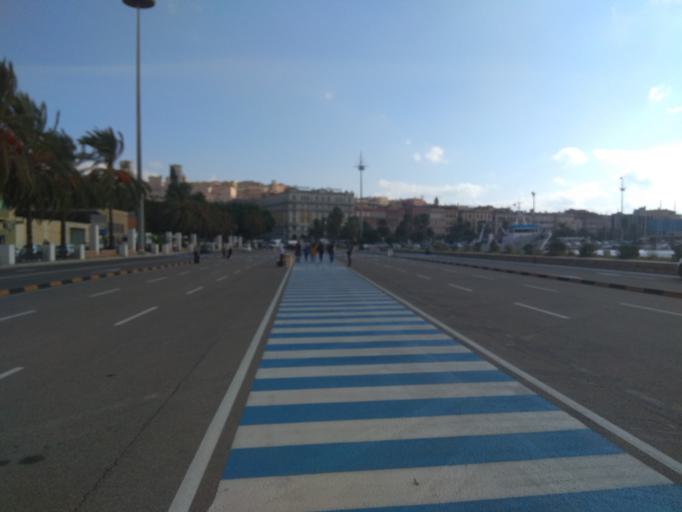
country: IT
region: Sardinia
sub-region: Provincia di Cagliari
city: Cagliari
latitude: 39.2138
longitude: 9.1081
